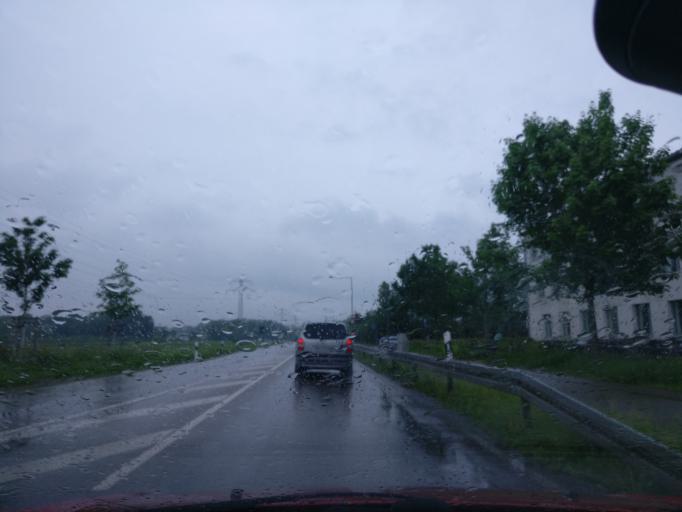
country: DE
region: Bavaria
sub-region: Upper Bavaria
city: Dachau
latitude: 48.2493
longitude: 11.4549
